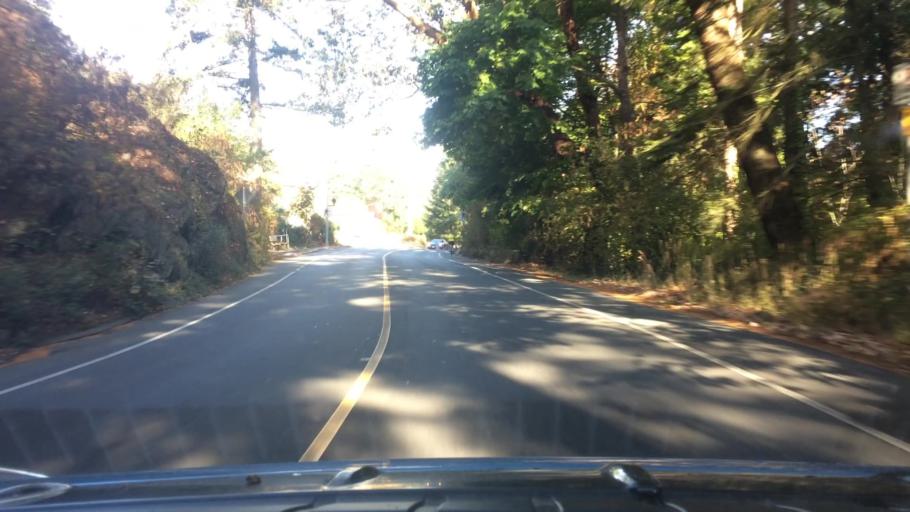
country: CA
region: British Columbia
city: Oak Bay
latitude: 48.5015
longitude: -123.3428
